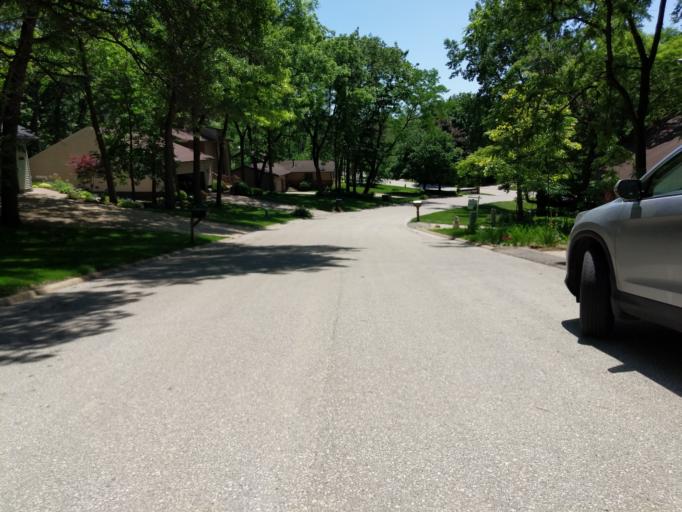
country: US
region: Iowa
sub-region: Linn County
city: Cedar Rapids
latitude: 42.0198
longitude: -91.6243
